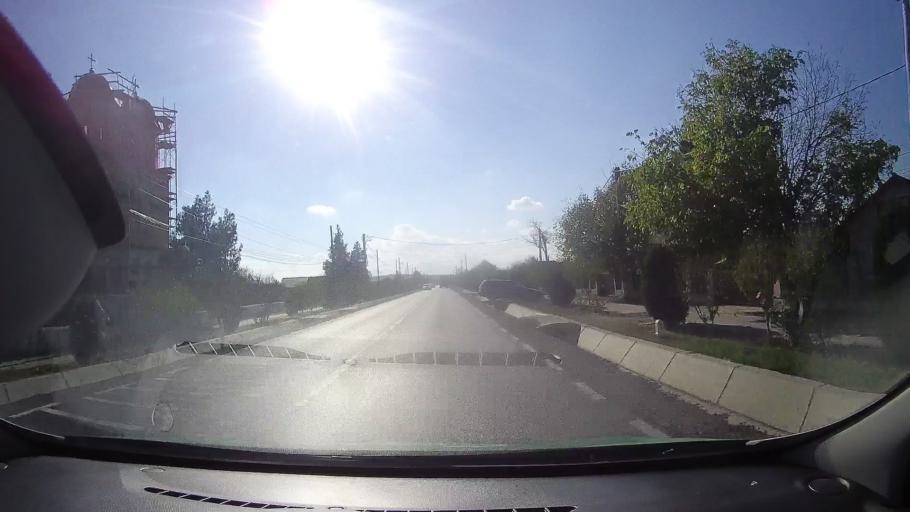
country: RO
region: Tulcea
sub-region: Comuna Baia
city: Baia
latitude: 44.7324
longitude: 28.6820
